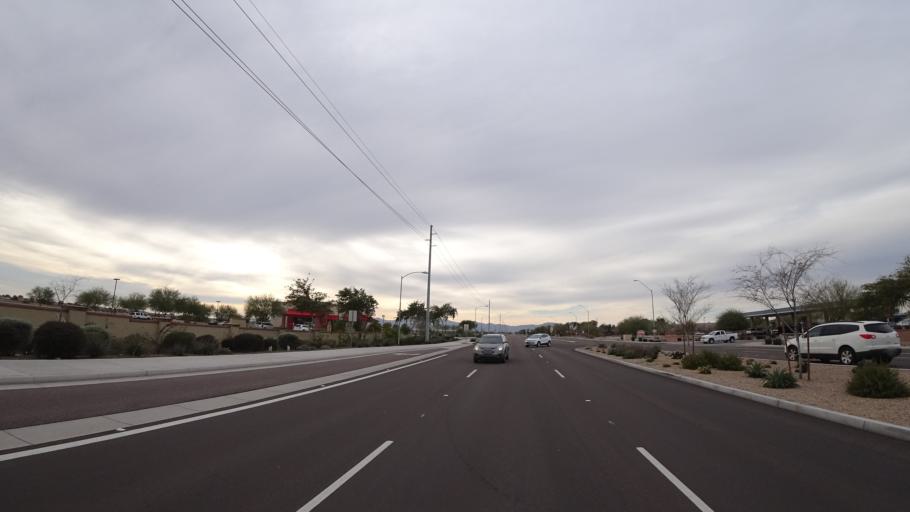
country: US
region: Arizona
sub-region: Maricopa County
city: Surprise
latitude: 33.6091
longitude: -112.3613
